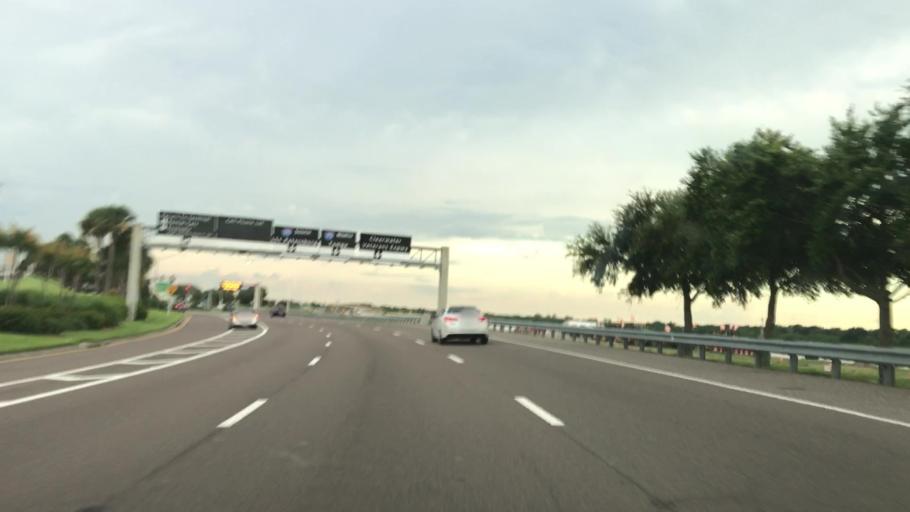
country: US
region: Florida
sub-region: Hillsborough County
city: Town 'n' Country
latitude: 27.9705
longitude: -82.5397
